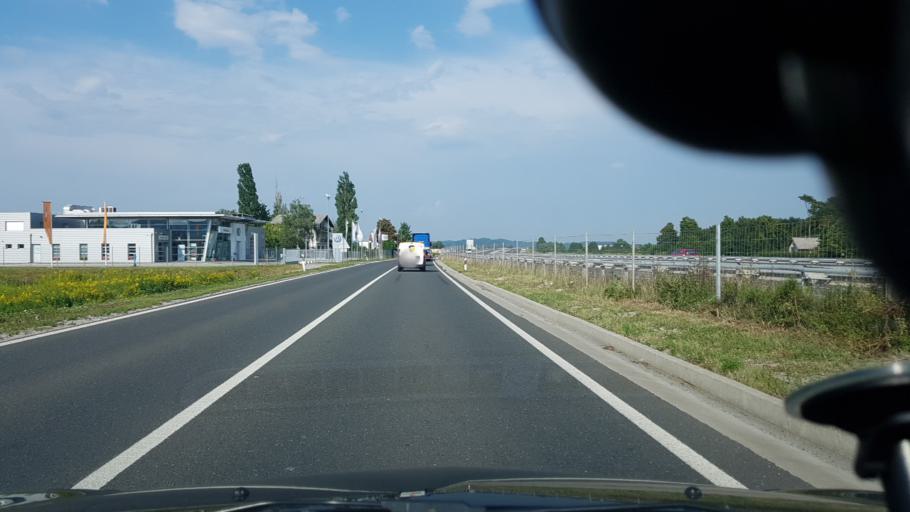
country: HR
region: Krapinsko-Zagorska
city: Oroslavje
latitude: 46.0035
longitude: 15.8700
